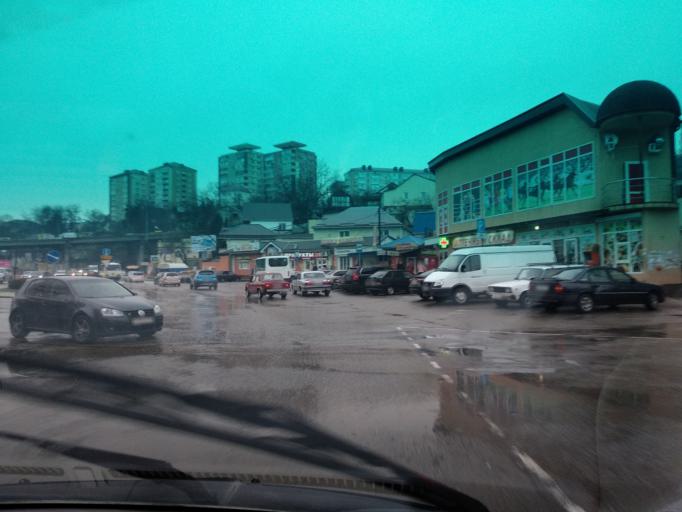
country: RU
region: Krasnodarskiy
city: Tuapse
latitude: 44.1064
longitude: 39.0874
